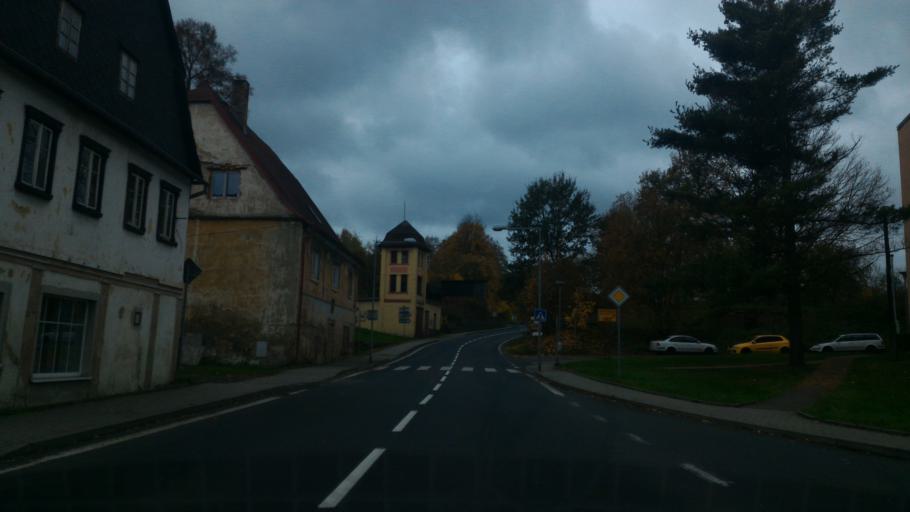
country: CZ
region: Ustecky
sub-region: Okres Decin
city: Chribska
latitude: 50.8626
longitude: 14.4814
